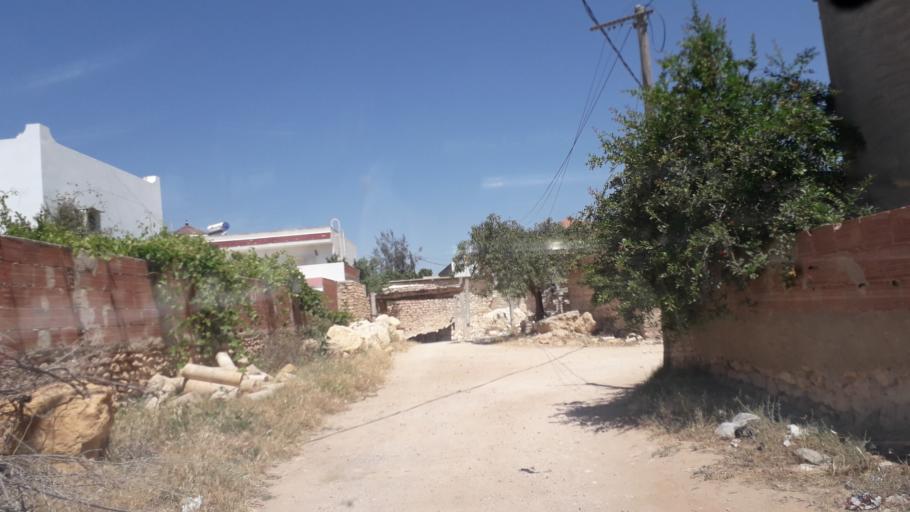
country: TN
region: Safaqis
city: Al Qarmadah
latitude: 34.8273
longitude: 10.7686
